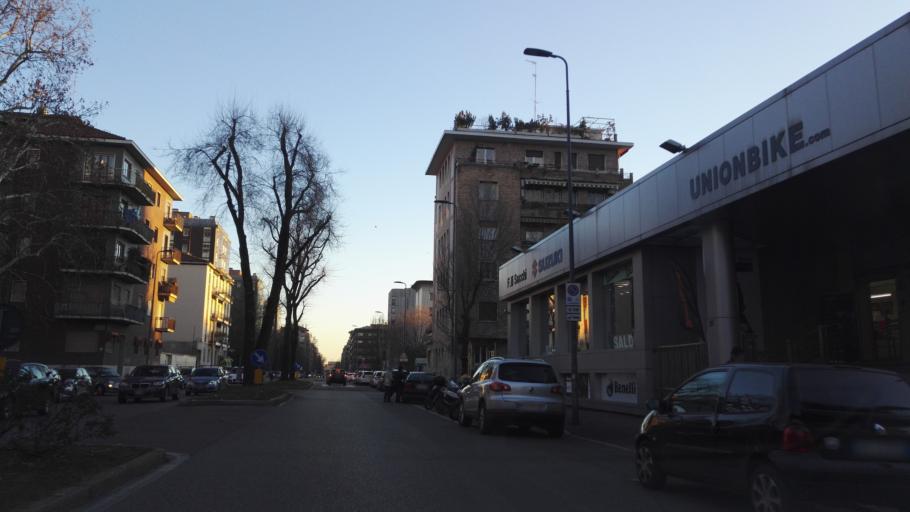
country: IT
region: Lombardy
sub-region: Citta metropolitana di Milano
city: Romano Banco
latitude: 45.4578
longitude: 9.1473
